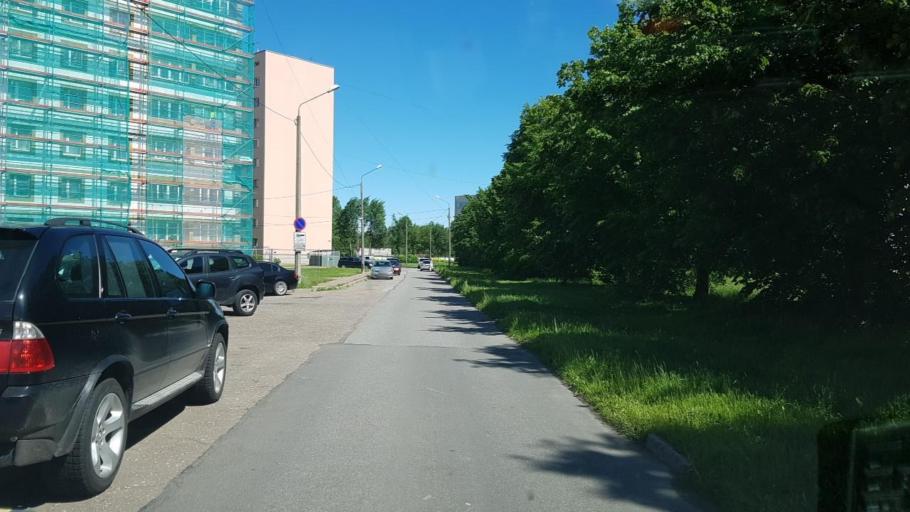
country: EE
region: Ida-Virumaa
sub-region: Narva linn
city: Narva
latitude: 59.3913
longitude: 28.1761
